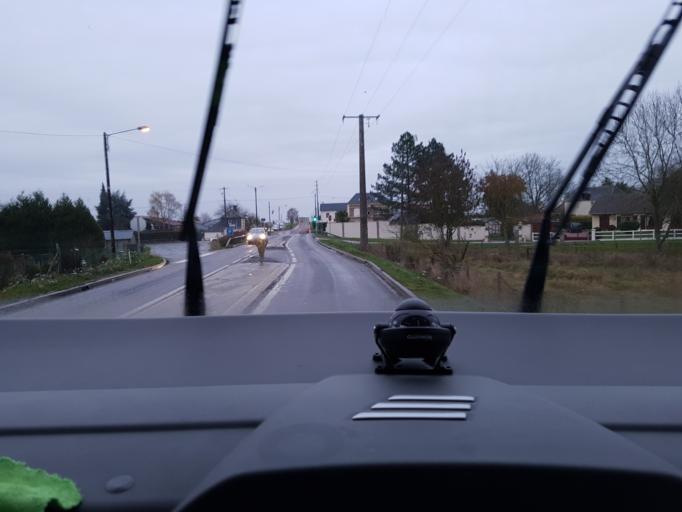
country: FR
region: Haute-Normandie
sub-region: Departement de l'Eure
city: Le Neubourg
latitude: 49.1480
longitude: 0.9667
